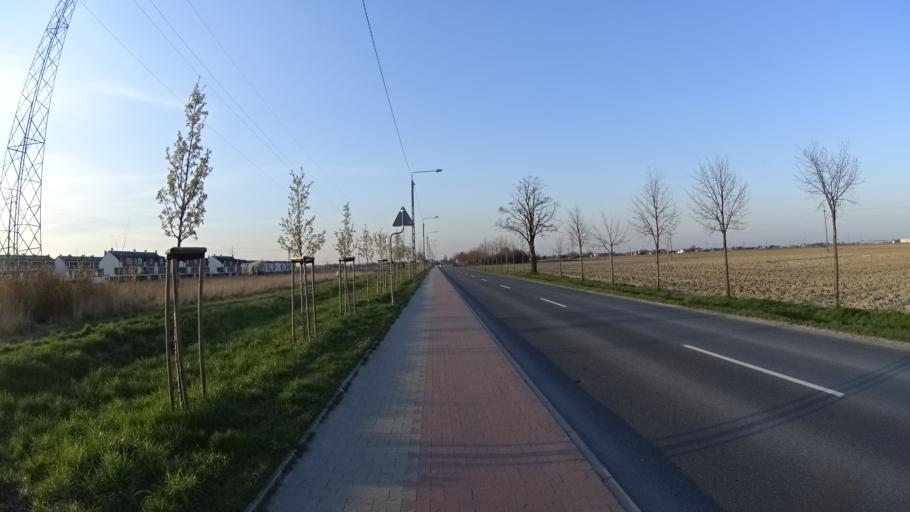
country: PL
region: Masovian Voivodeship
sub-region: Powiat warszawski zachodni
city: Ozarow Mazowiecki
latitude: 52.2142
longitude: 20.8114
